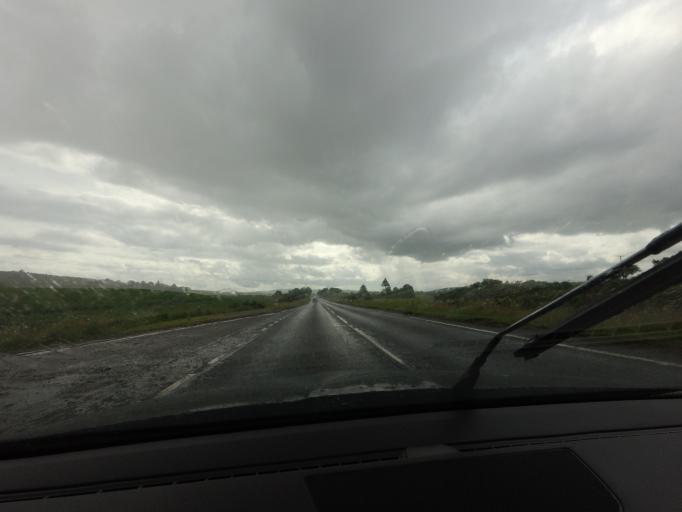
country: GB
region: Scotland
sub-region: Highland
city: Fortrose
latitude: 57.5137
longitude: -4.0927
